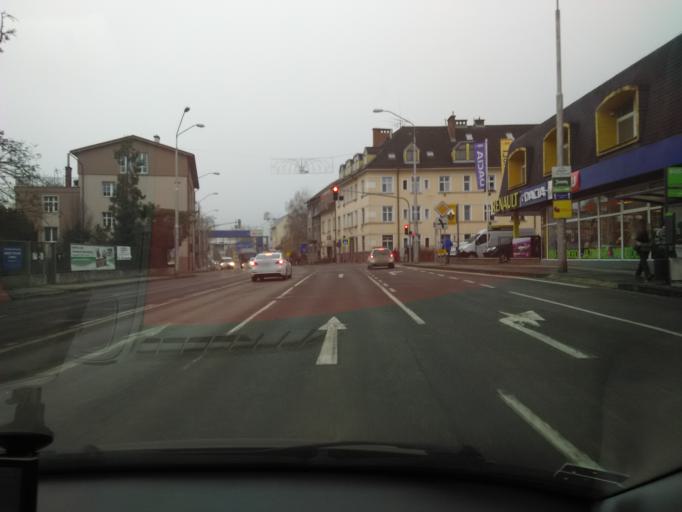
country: SK
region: Trenciansky
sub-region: Okres Trencin
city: Trencin
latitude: 48.8923
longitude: 18.0532
